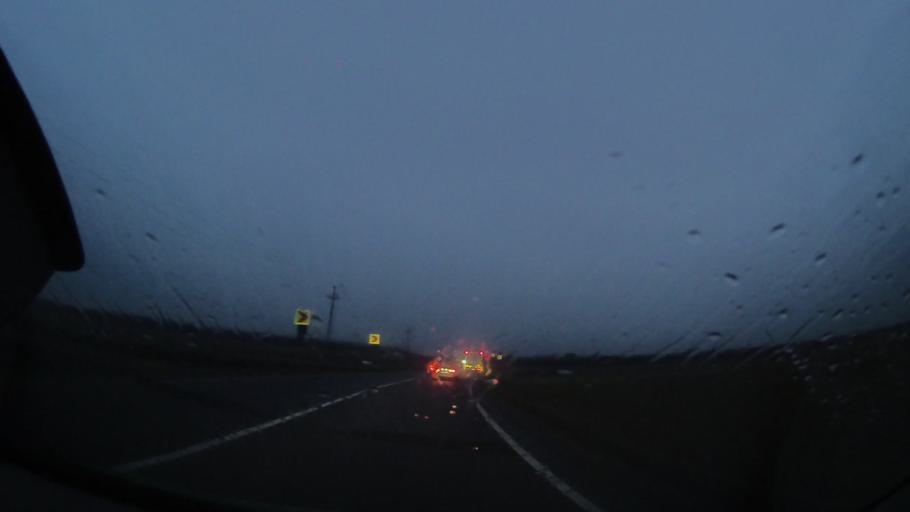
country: RO
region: Harghita
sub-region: Comuna Ditrau
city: Ditrau
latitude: 46.8198
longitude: 25.4919
